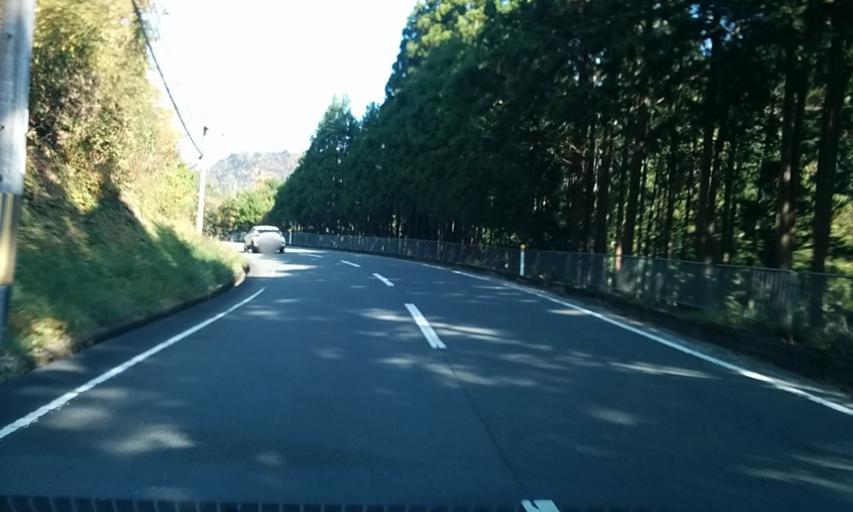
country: JP
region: Fukui
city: Obama
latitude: 35.2835
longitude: 135.5937
